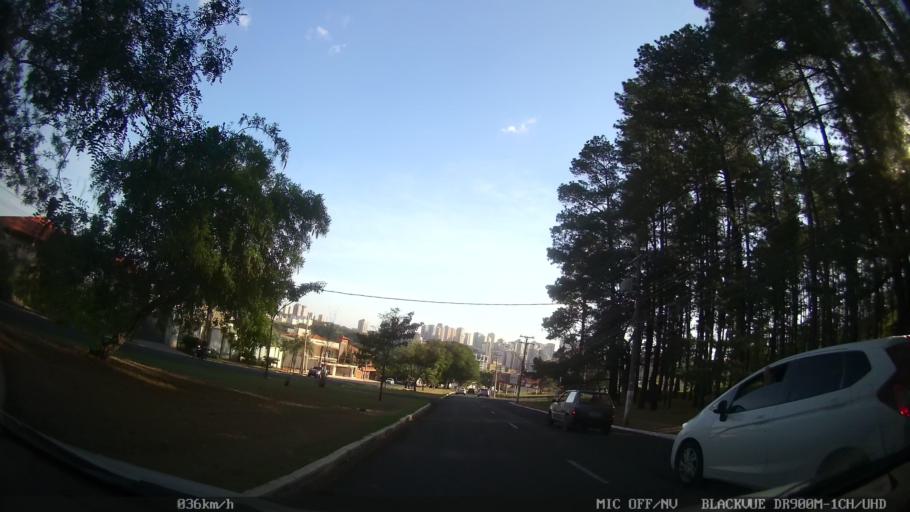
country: BR
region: Sao Paulo
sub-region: Ribeirao Preto
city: Ribeirao Preto
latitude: -21.2053
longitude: -47.7844
